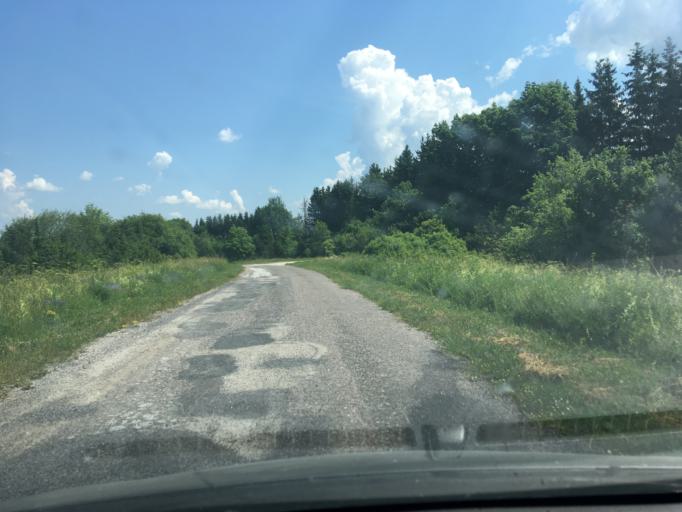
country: EE
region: Laeaene
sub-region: Lihula vald
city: Lihula
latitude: 58.6666
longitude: 23.7608
